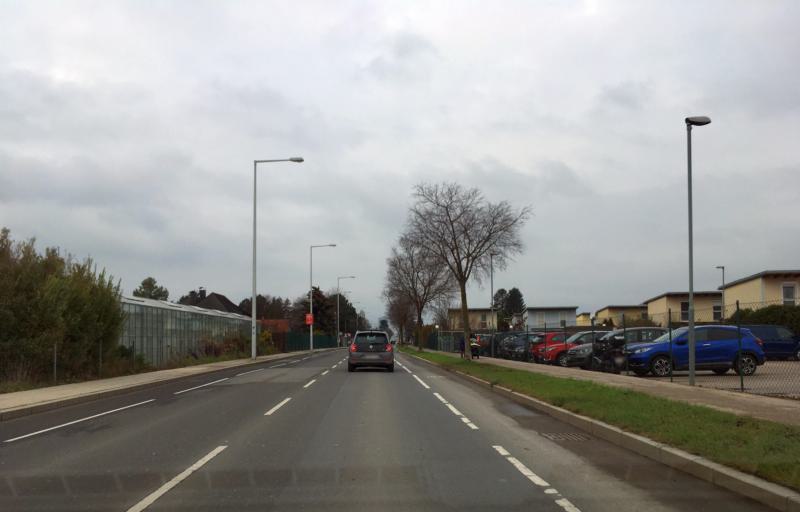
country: AT
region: Lower Austria
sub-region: Politischer Bezirk Wien-Umgebung
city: Gerasdorf bei Wien
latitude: 48.2556
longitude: 16.4927
